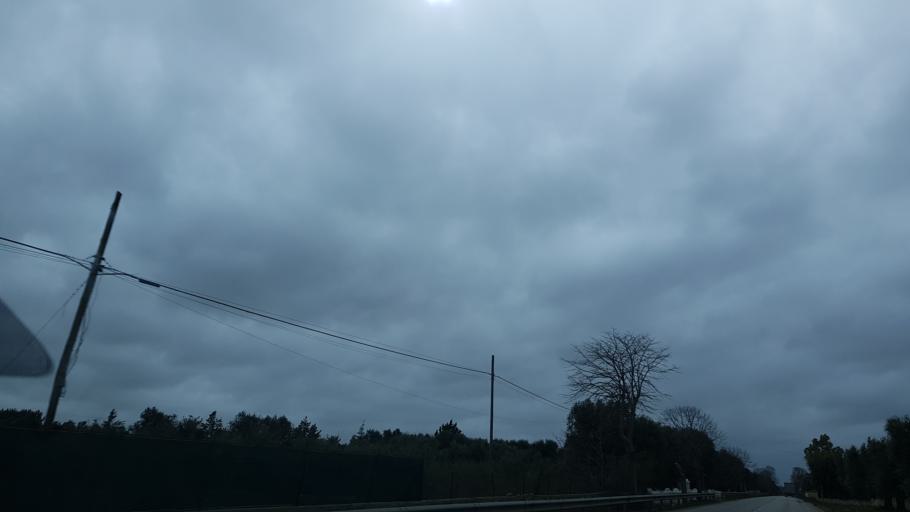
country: IT
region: Apulia
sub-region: Provincia di Brindisi
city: San Vito dei Normanni
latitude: 40.6551
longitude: 17.7592
